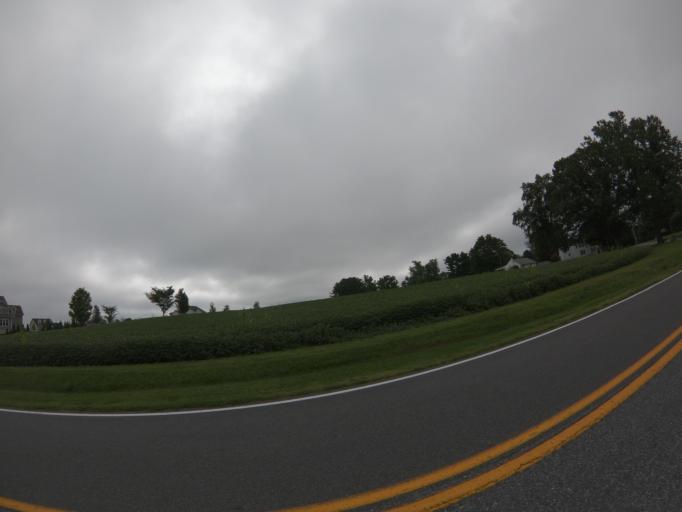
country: US
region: Maryland
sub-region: Carroll County
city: Mount Airy
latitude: 39.3187
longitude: -77.1194
